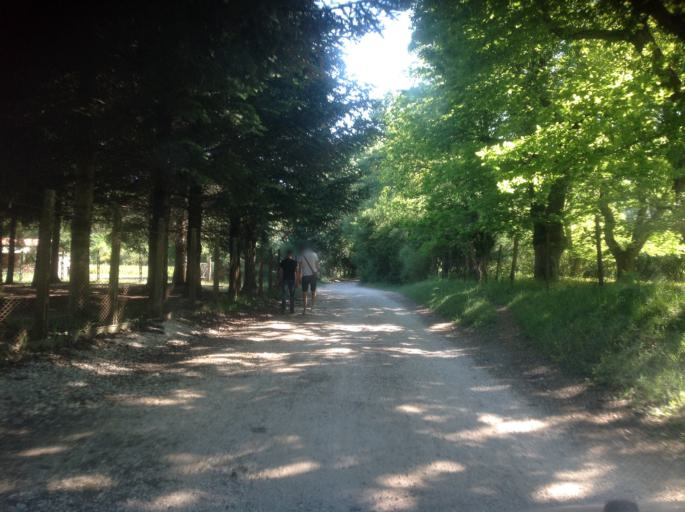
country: IT
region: Latium
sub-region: Provincia di Rieti
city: Limiti di Greccio
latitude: 42.4754
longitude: 12.7084
